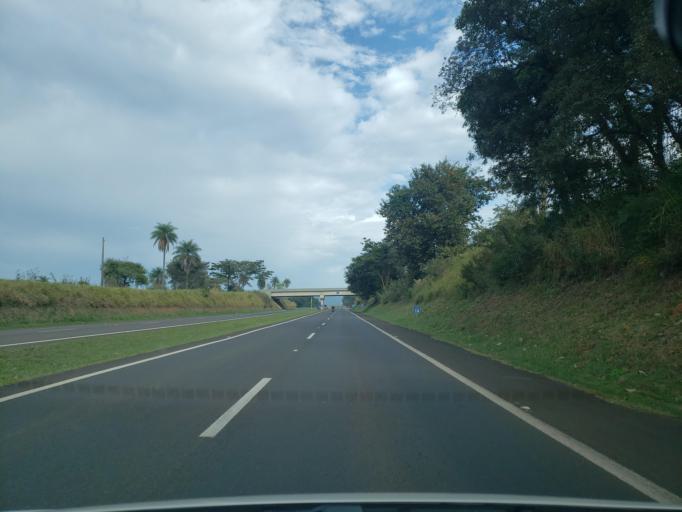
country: BR
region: Sao Paulo
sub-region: Brotas
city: Brotas
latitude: -22.2632
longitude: -48.1895
